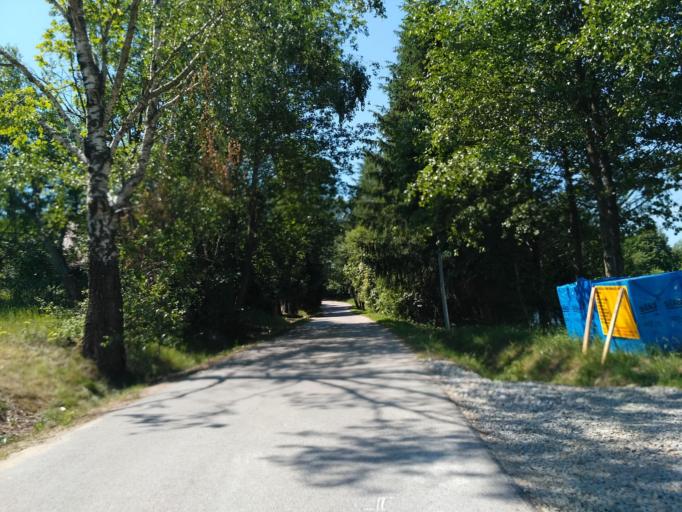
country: PL
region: Subcarpathian Voivodeship
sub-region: Krosno
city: Krosno
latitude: 49.7097
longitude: 21.7728
